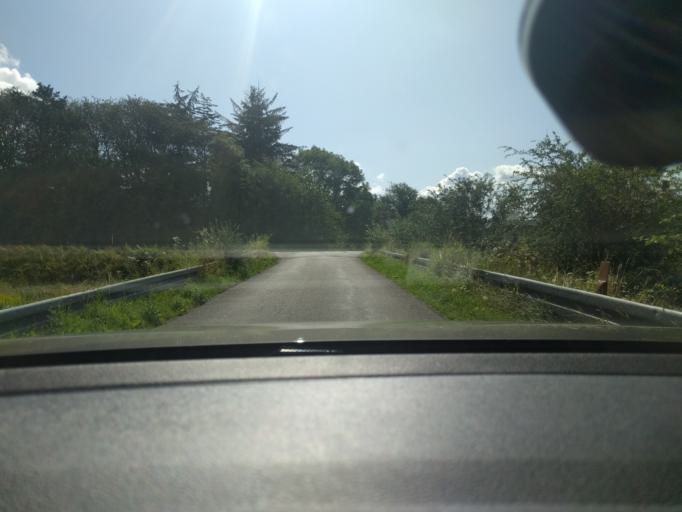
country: DK
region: Central Jutland
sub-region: Viborg Kommune
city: Bjerringbro
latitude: 56.5020
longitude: 9.5848
